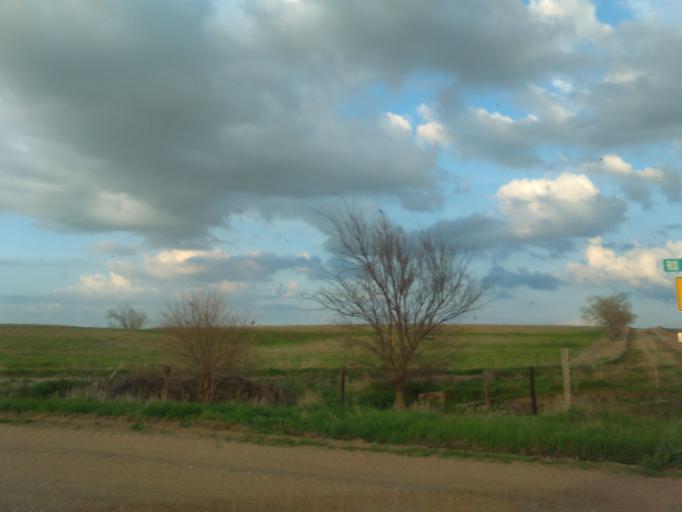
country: US
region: Nebraska
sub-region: Webster County
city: Red Cloud
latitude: 40.2054
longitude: -98.3681
